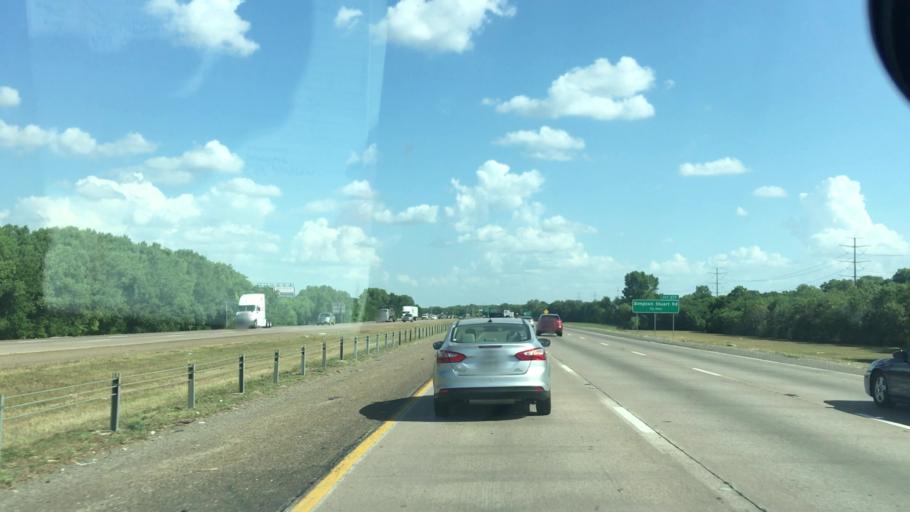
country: US
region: Texas
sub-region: Dallas County
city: Hutchins
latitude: 32.6935
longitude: -96.7503
